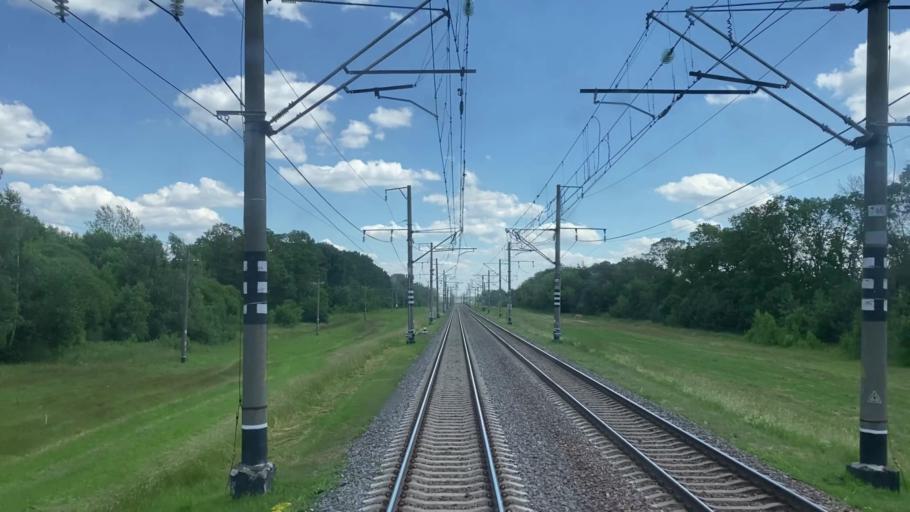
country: BY
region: Brest
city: Ivatsevichy
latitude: 52.8361
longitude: 25.5120
